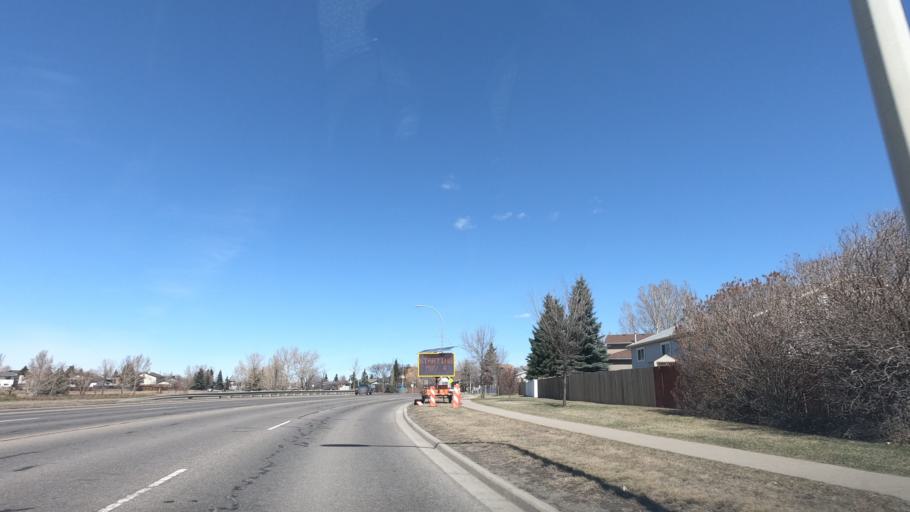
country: CA
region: Alberta
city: Airdrie
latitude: 51.2822
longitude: -114.0108
